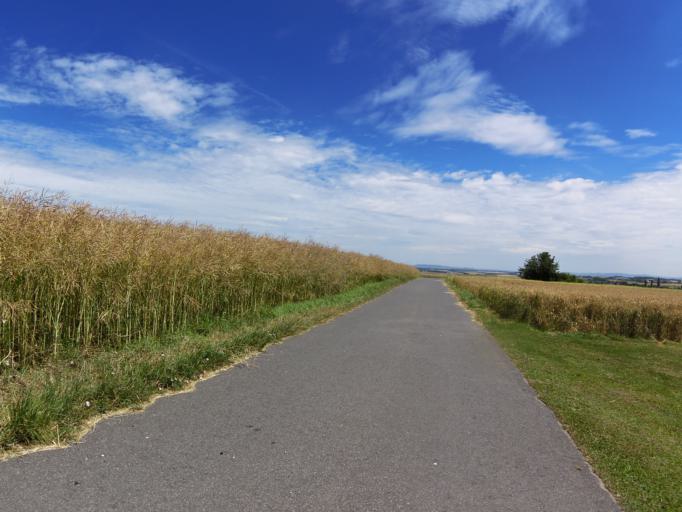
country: DE
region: Bavaria
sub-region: Regierungsbezirk Unterfranken
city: Geroldshausen
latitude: 49.7060
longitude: 9.8915
